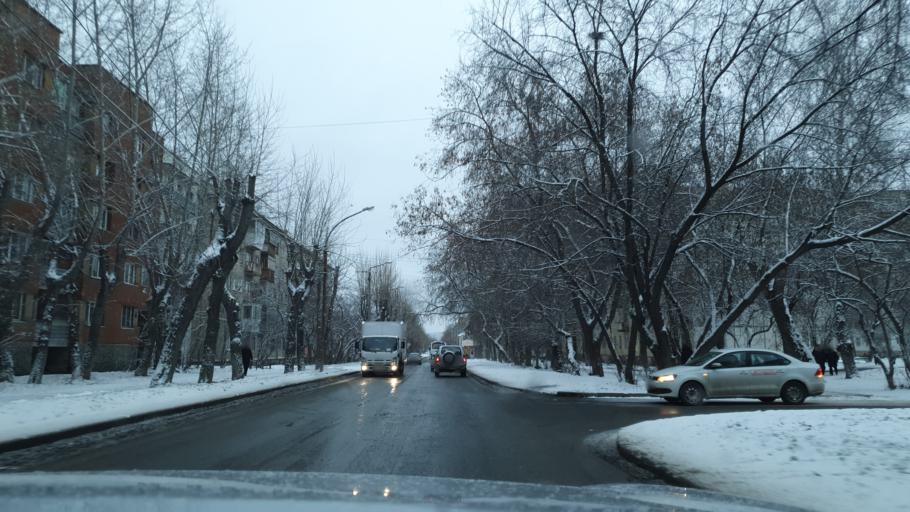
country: RU
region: Sverdlovsk
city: Istok
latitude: 56.7521
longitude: 60.7089
